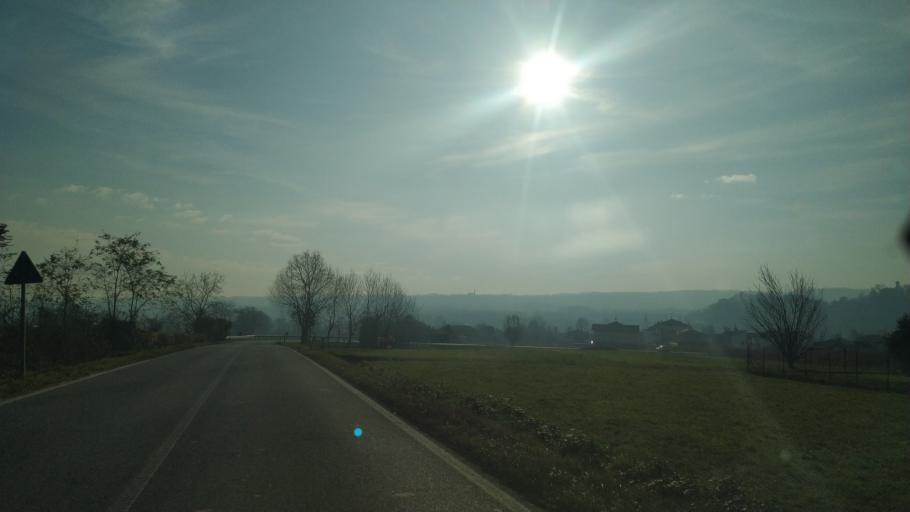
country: IT
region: Piedmont
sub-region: Provincia di Biella
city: Mongrando
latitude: 45.5268
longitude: 8.0136
